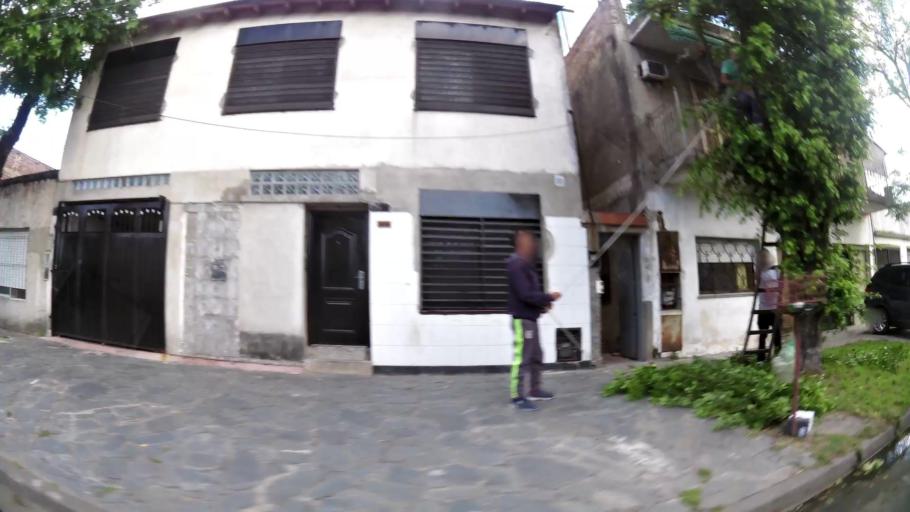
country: AR
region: Buenos Aires
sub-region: Partido de Avellaneda
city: Avellaneda
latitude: -34.6752
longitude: -58.3588
